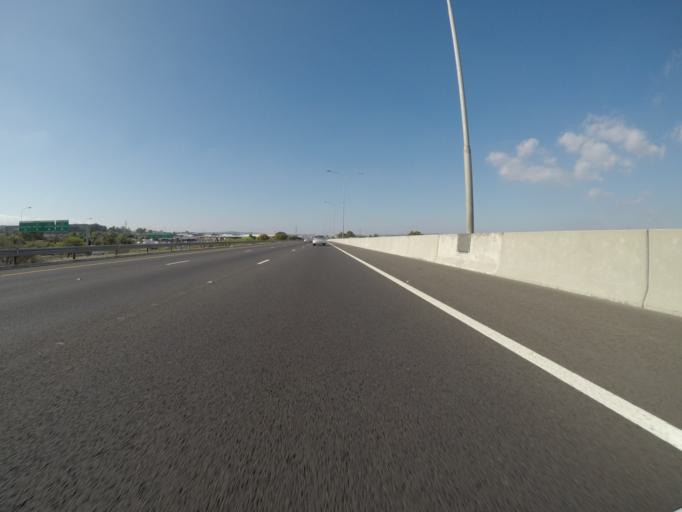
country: ZA
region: Western Cape
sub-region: City of Cape Town
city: Kraaifontein
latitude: -33.9157
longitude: 18.6676
